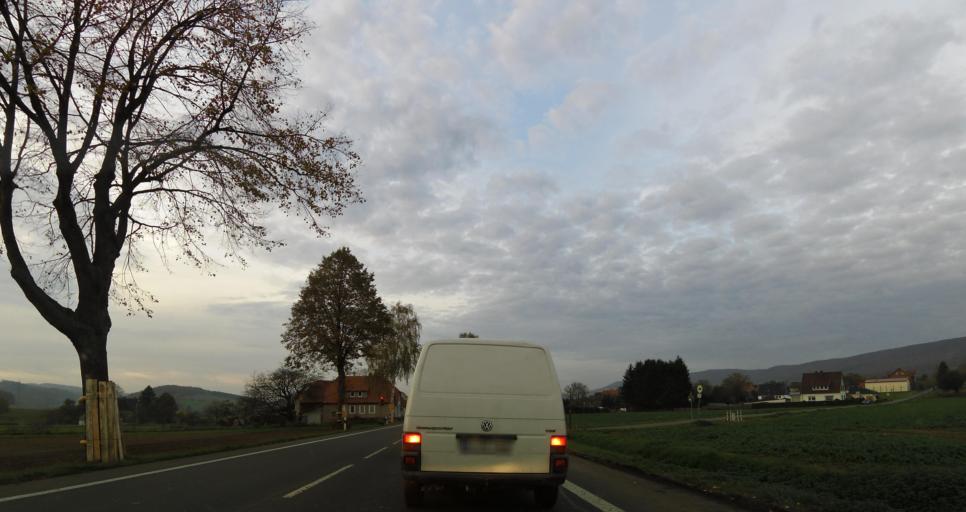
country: DE
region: Lower Saxony
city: Luerdissen
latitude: 51.9470
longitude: 9.6243
